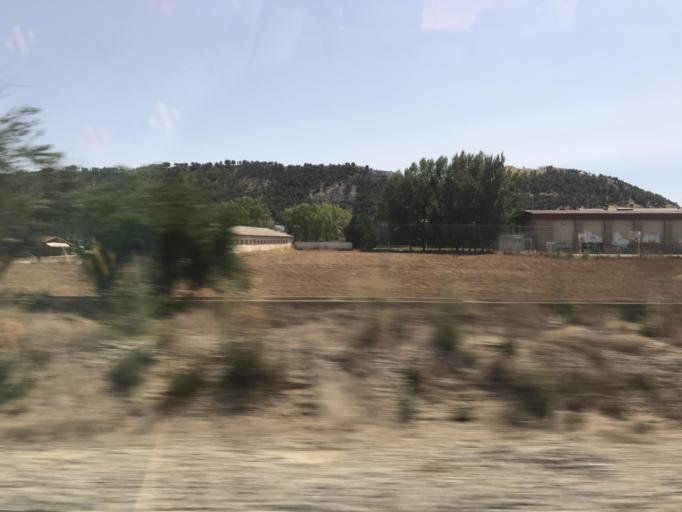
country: ES
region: Castille and Leon
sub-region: Provincia de Valladolid
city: Cabezon
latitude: 41.7424
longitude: -4.6468
